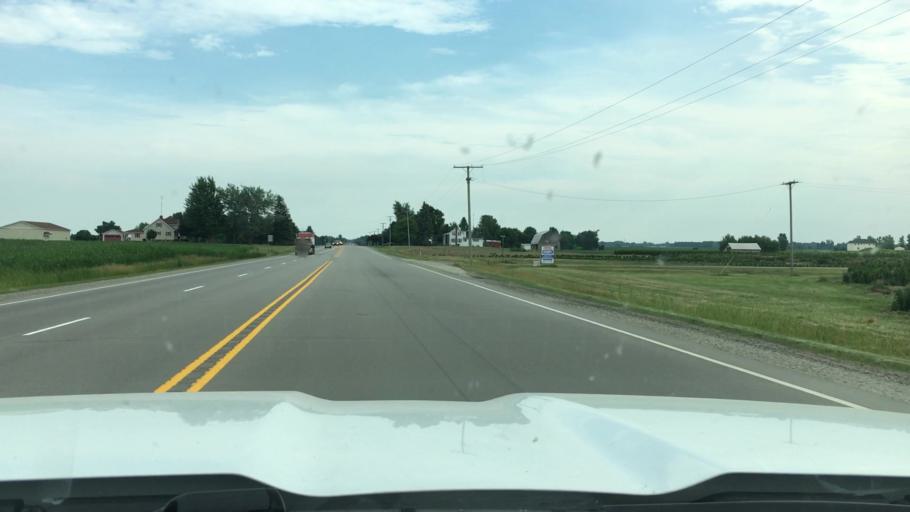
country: US
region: Michigan
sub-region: Sanilac County
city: Marlette
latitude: 43.3777
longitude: -83.0858
